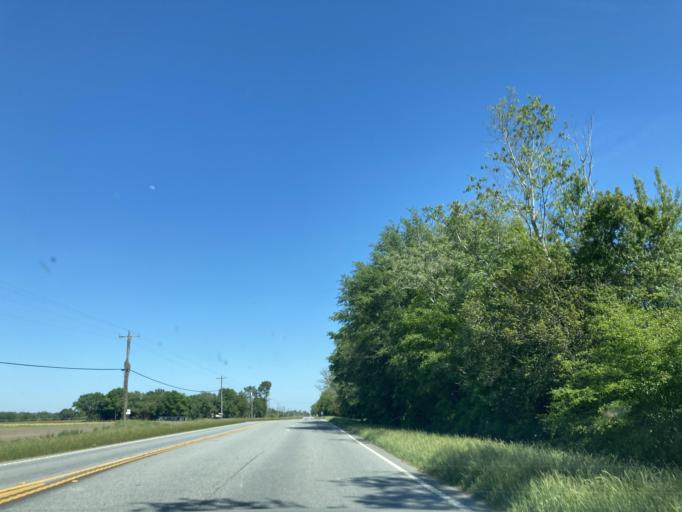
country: US
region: Georgia
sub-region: Miller County
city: Colquitt
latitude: 31.1853
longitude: -84.6018
